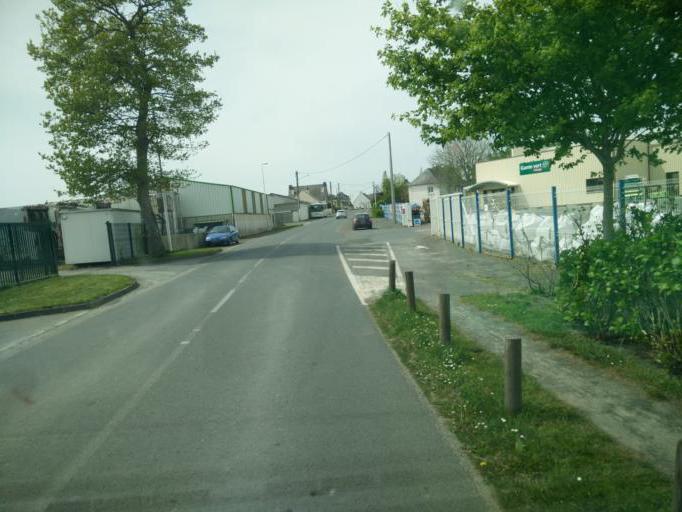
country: FR
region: Brittany
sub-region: Departement des Cotes-d'Armor
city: Matignon
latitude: 48.5939
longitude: -2.2830
